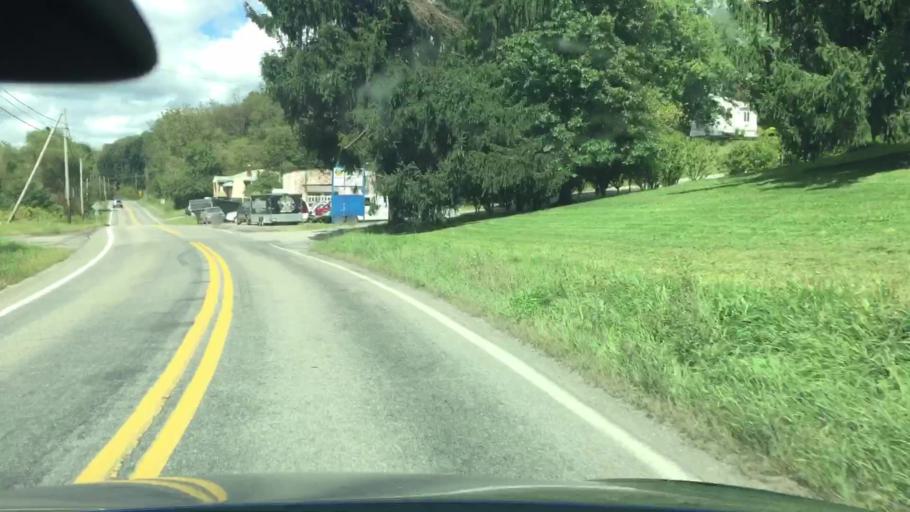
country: US
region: Pennsylvania
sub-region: Allegheny County
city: Russellton
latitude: 40.6280
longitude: -79.8329
